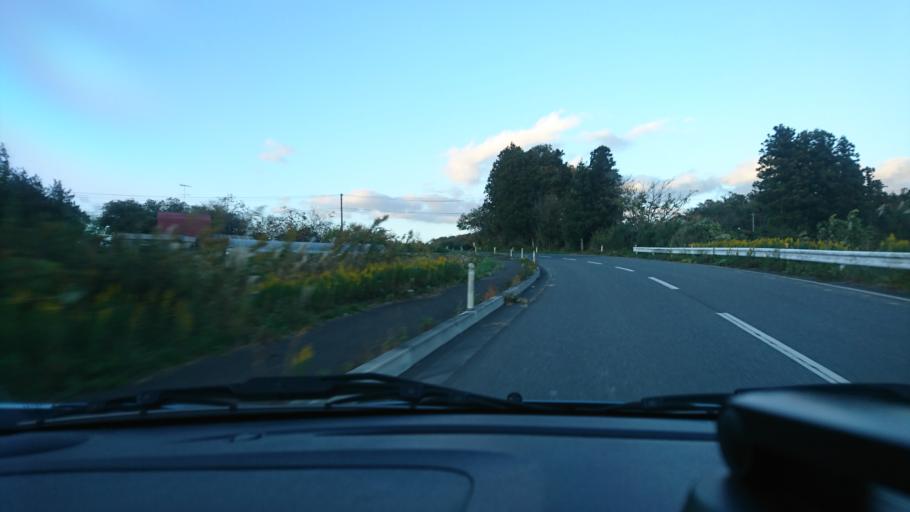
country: JP
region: Iwate
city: Ichinoseki
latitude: 38.7687
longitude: 141.2396
